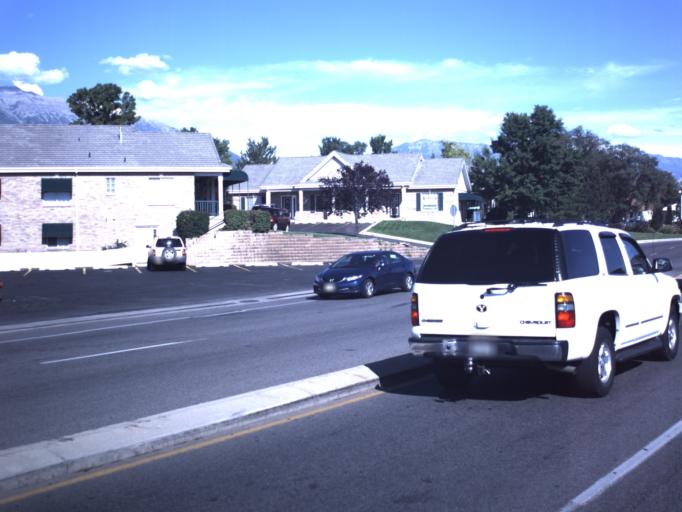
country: US
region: Utah
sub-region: Utah County
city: American Fork
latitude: 40.3778
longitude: -111.8126
